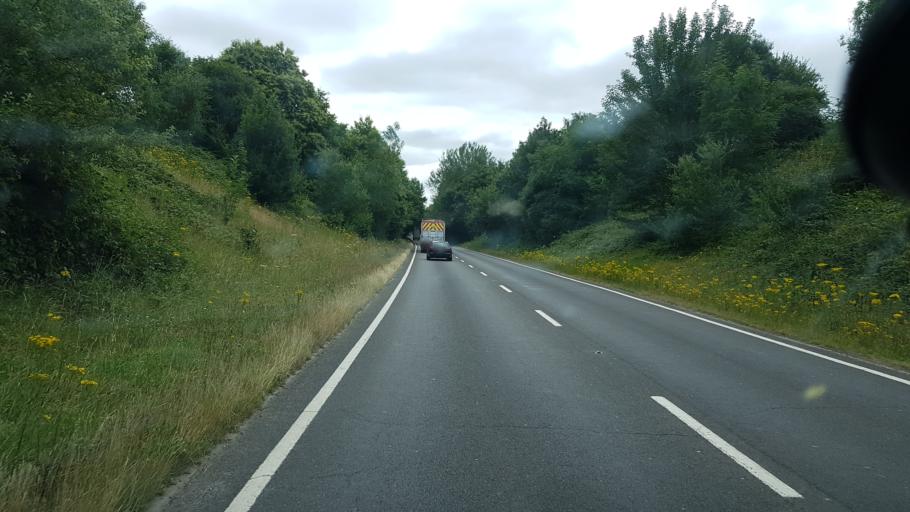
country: GB
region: England
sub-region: Surrey
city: Godstone
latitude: 51.2470
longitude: -0.0516
